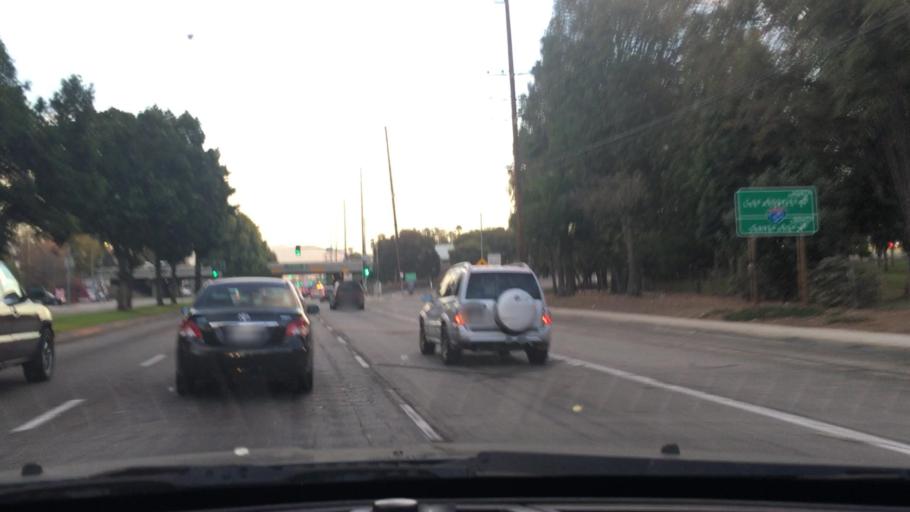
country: US
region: California
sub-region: Los Angeles County
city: Downey
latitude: 33.9562
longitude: -118.1126
